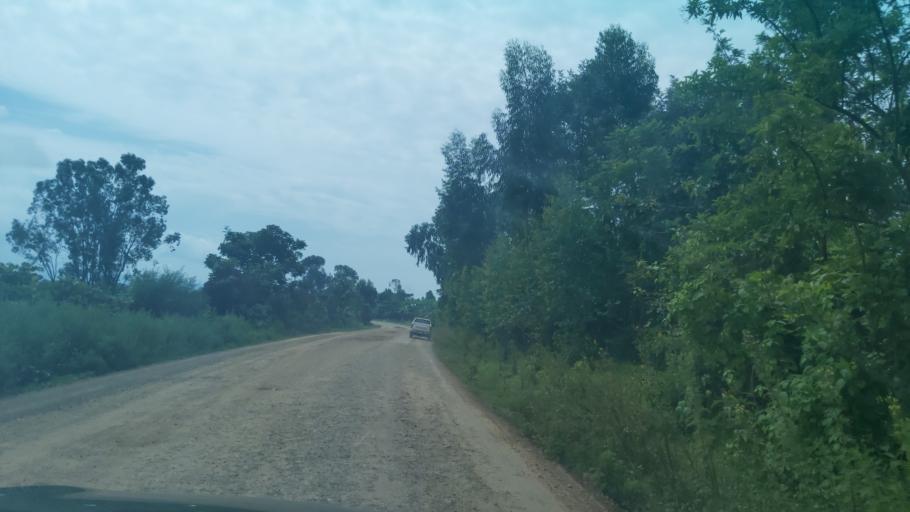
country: ET
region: Oromiya
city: Jima
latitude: 7.7409
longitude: 36.7859
